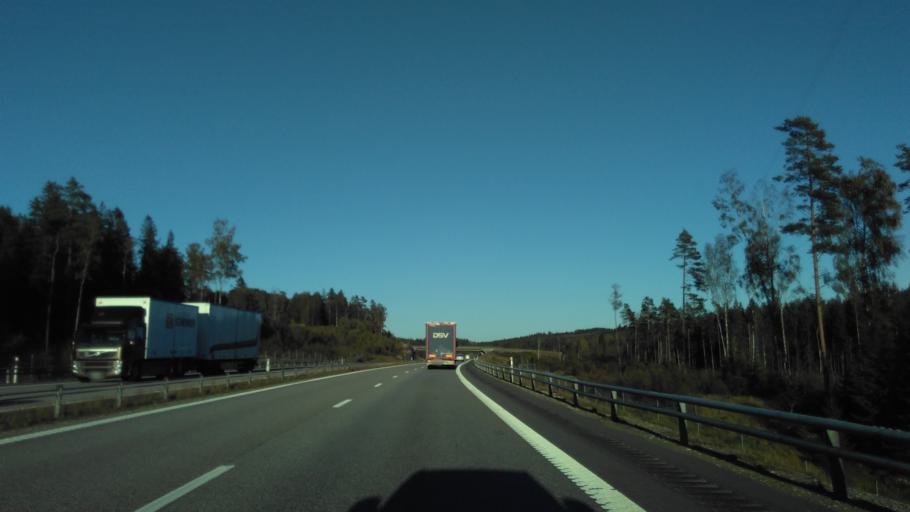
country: SE
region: Vaestra Goetaland
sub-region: Boras Kommun
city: Dalsjofors
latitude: 57.7391
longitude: 13.0482
